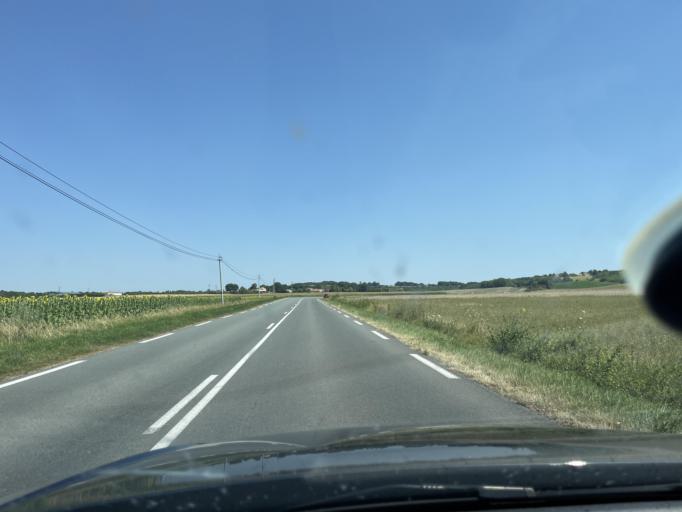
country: FR
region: Poitou-Charentes
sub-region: Departement de la Charente-Maritime
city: Mirambeau
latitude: 45.4174
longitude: -0.6253
